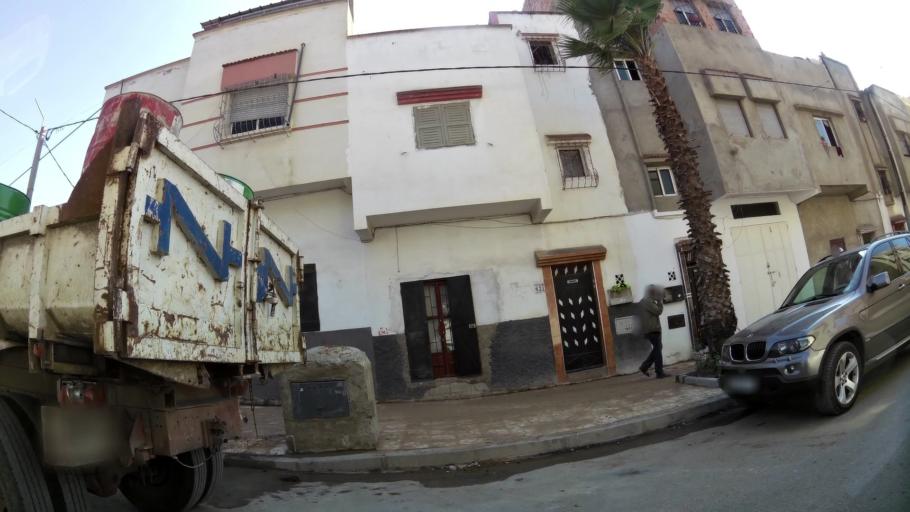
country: MA
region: Rabat-Sale-Zemmour-Zaer
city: Sale
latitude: 34.0562
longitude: -6.7720
